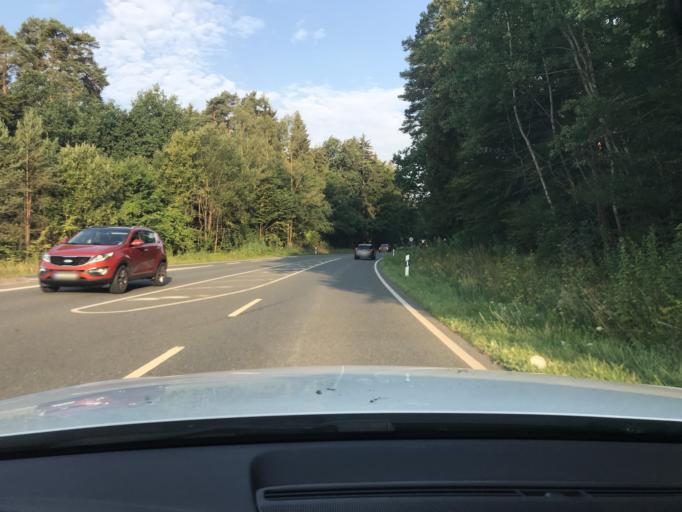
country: DE
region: Bavaria
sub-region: Regierungsbezirk Mittelfranken
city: Schnaittach
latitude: 49.5666
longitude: 11.3254
